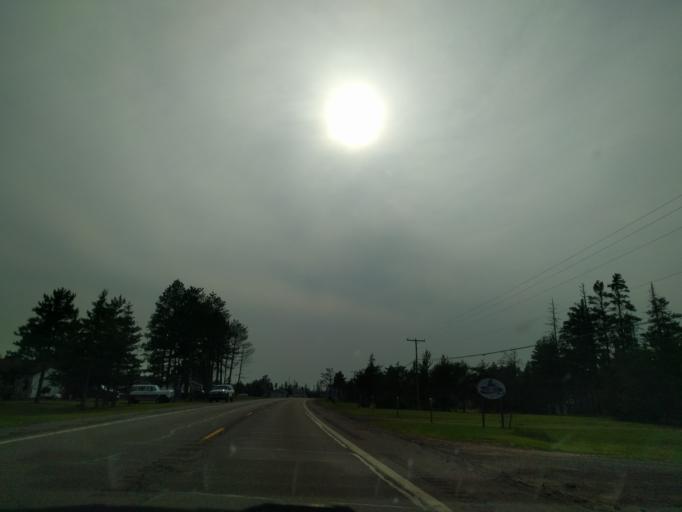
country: US
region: Michigan
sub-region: Marquette County
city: Gwinn
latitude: 46.2761
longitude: -87.4015
